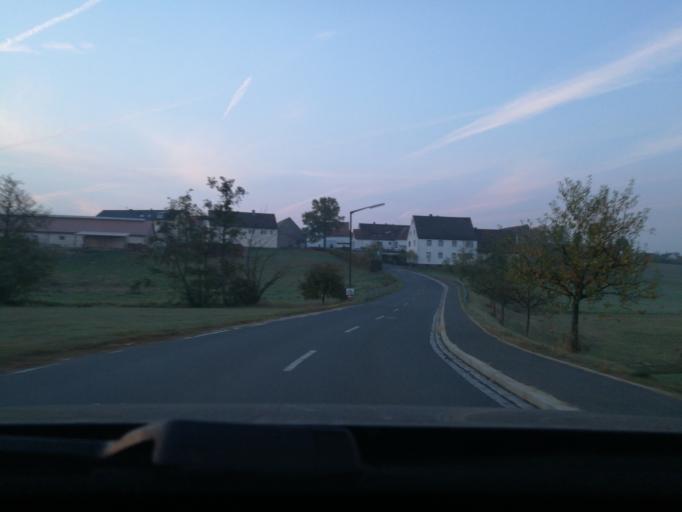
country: DE
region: Bavaria
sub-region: Regierungsbezirk Mittelfranken
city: Seukendorf
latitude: 49.4843
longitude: 10.8912
